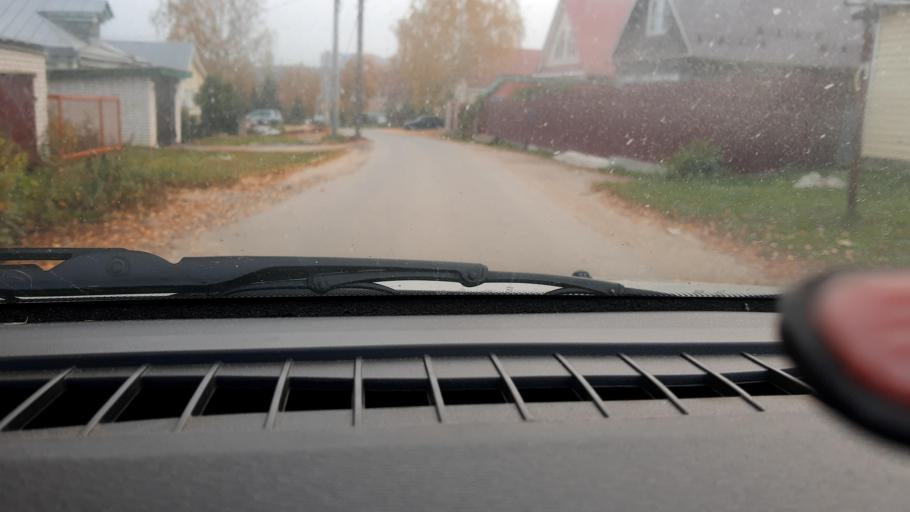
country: RU
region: Nizjnij Novgorod
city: Afonino
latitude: 56.2682
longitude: 44.0570
